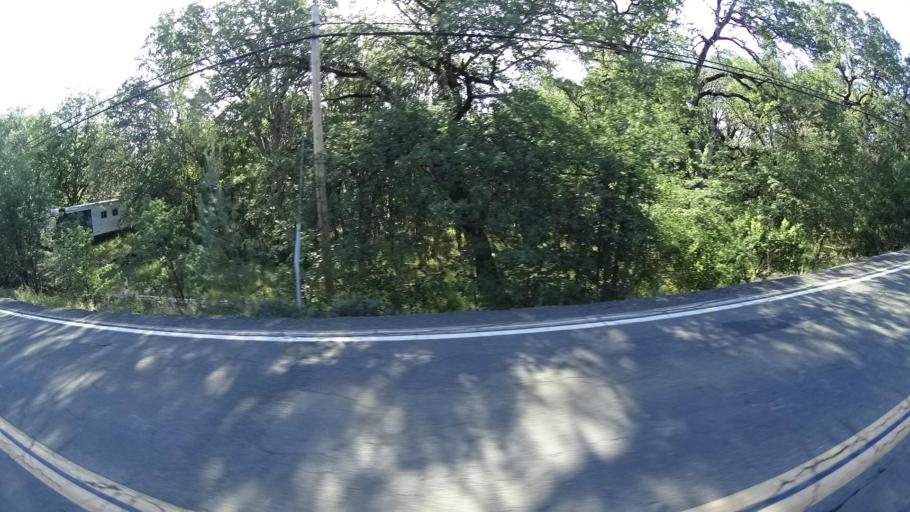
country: US
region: California
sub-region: Lake County
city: Lakeport
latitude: 39.0527
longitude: -122.9404
